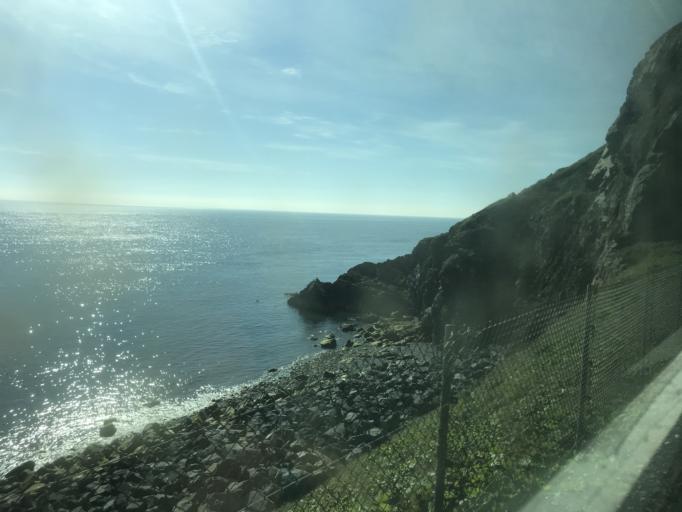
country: IE
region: Leinster
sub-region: Wicklow
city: Bray
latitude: 53.1834
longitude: -6.0769
